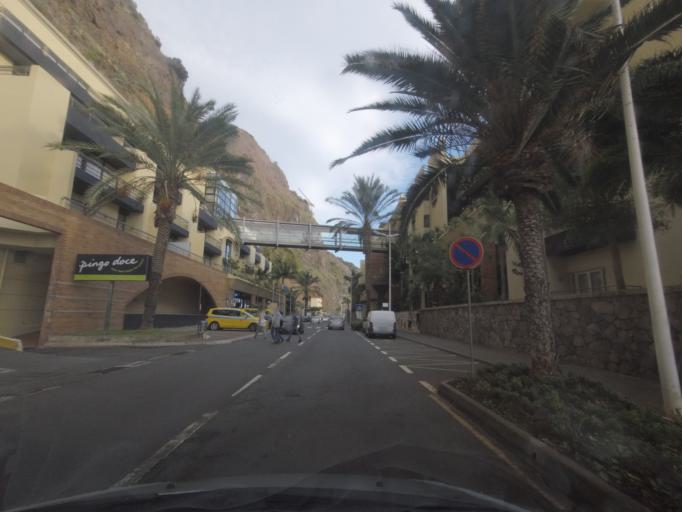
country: PT
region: Madeira
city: Calheta
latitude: 32.7196
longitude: -17.1743
